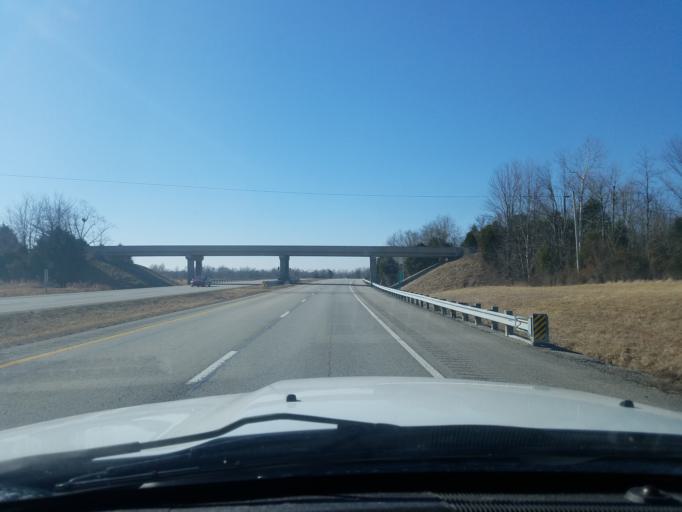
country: US
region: Kentucky
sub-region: Grayson County
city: Leitchfield
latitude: 37.4977
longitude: -86.1713
